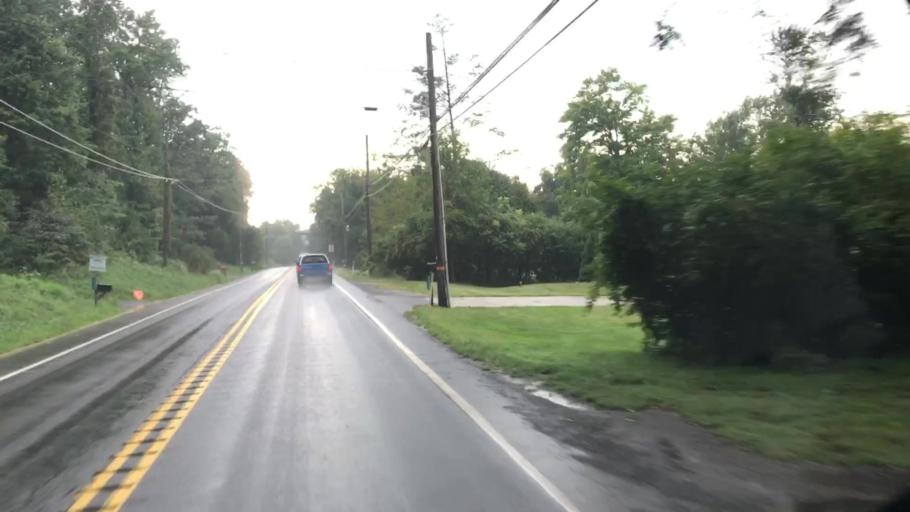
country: US
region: Pennsylvania
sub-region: Cumberland County
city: Schlusser
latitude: 40.2988
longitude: -77.1385
